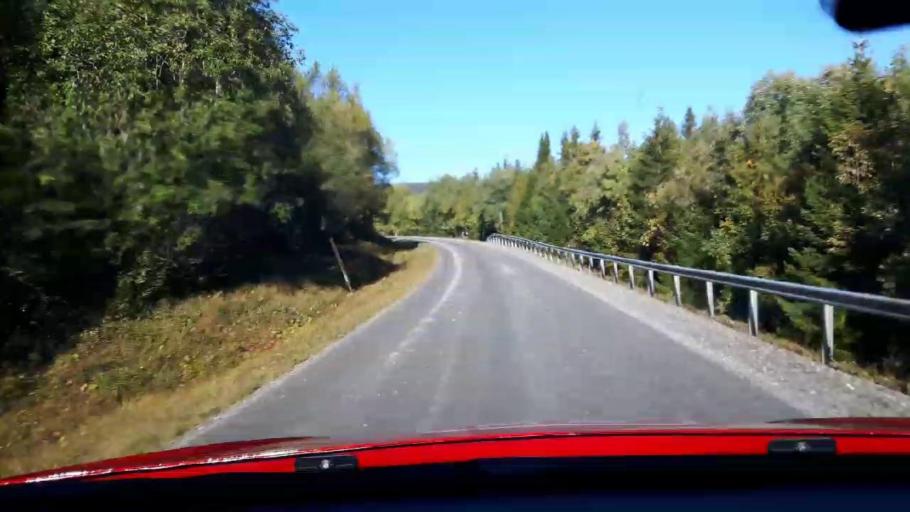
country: NO
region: Nord-Trondelag
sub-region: Lierne
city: Sandvika
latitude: 64.5849
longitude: 13.8846
